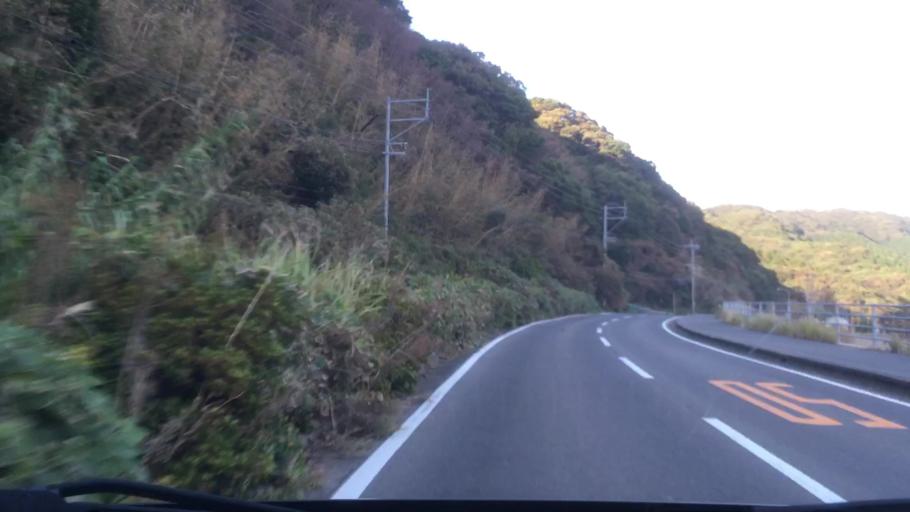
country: JP
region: Nagasaki
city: Sasebo
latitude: 33.0269
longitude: 129.6010
